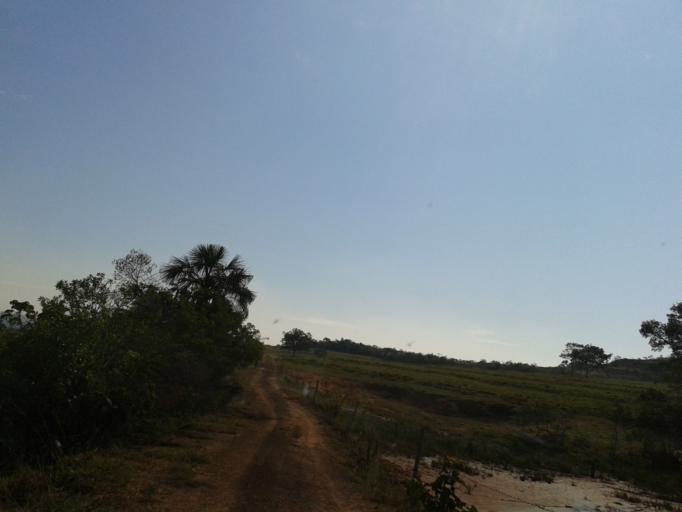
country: BR
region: Minas Gerais
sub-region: Campina Verde
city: Campina Verde
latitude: -19.3853
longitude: -49.6314
